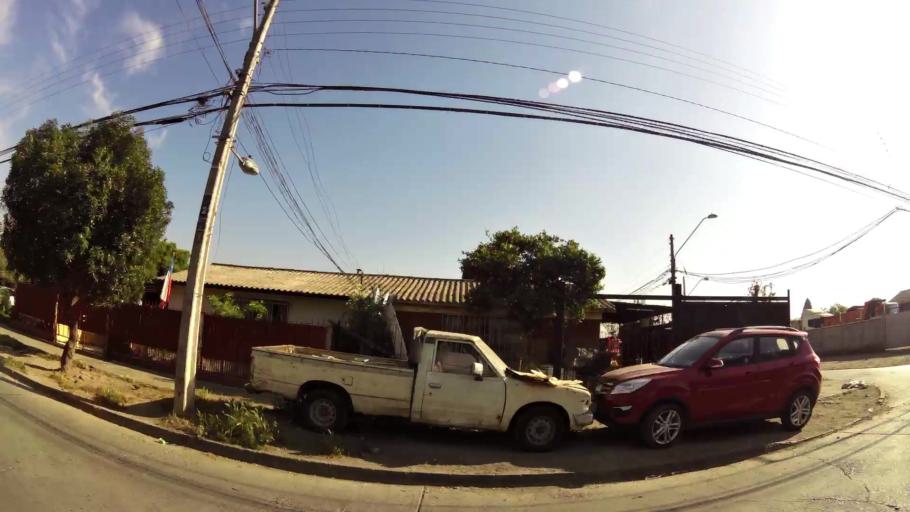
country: CL
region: Santiago Metropolitan
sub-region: Provincia de Santiago
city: La Pintana
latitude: -33.5632
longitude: -70.5938
